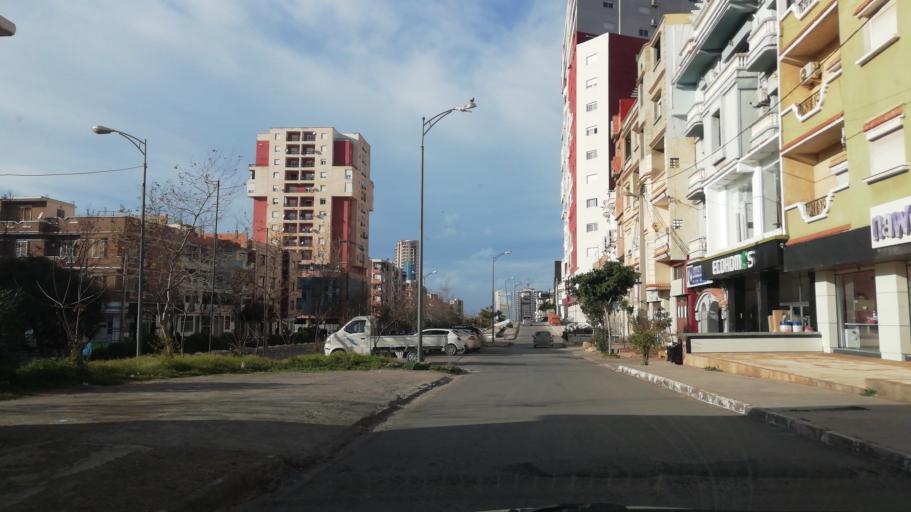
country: DZ
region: Oran
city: Bir el Djir
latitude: 35.7222
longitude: -0.5835
